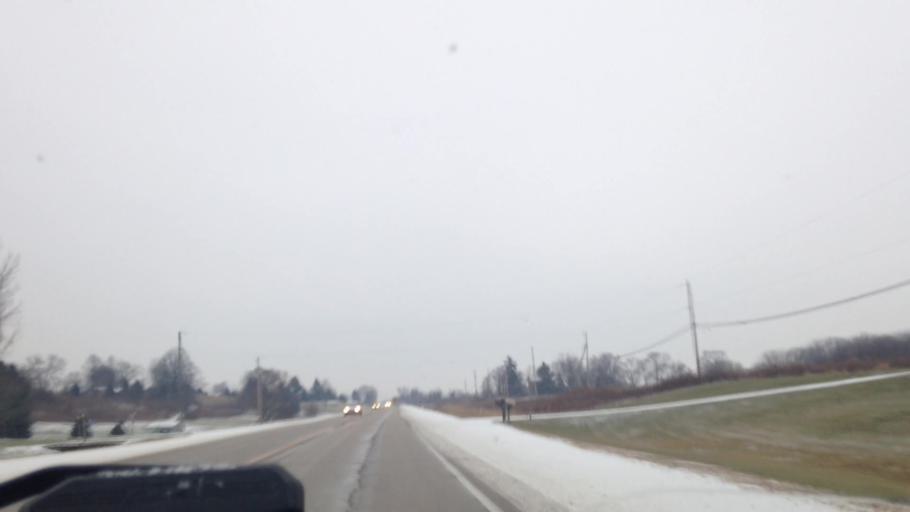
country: US
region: Wisconsin
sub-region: Dodge County
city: Mayville
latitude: 43.4352
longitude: -88.5420
